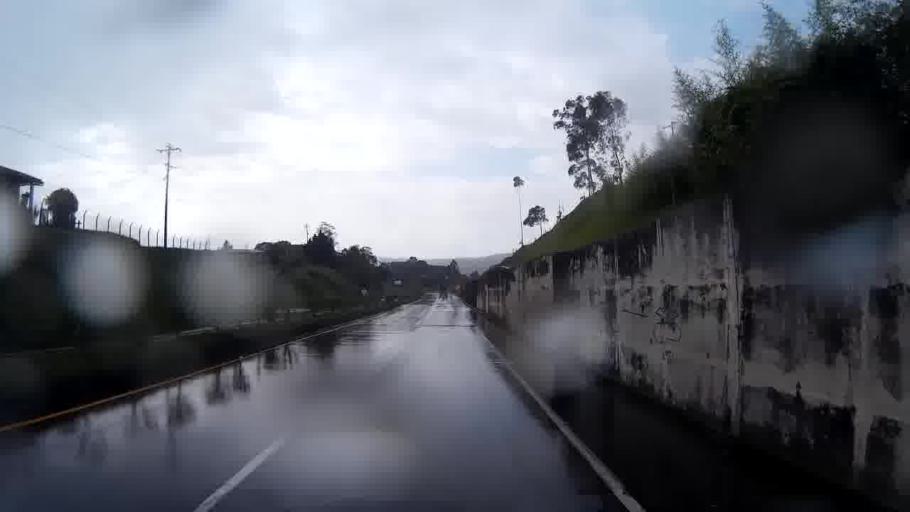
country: CO
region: Quindio
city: Salento
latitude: 4.6798
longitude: -75.6039
